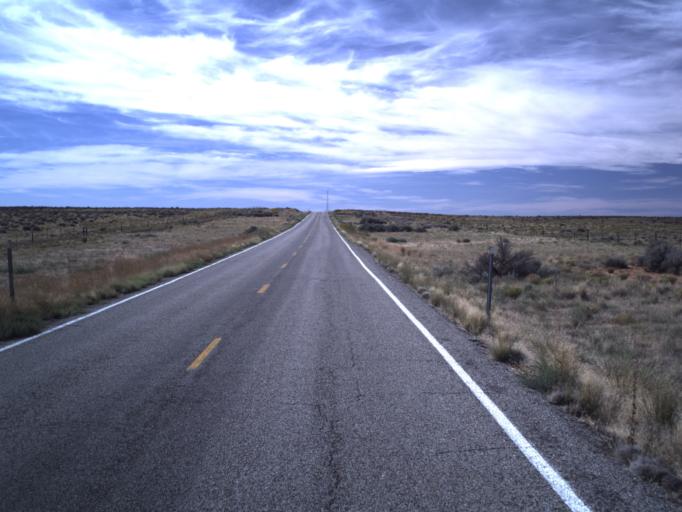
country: US
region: Utah
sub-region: San Juan County
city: Blanding
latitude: 37.3450
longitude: -109.3484
